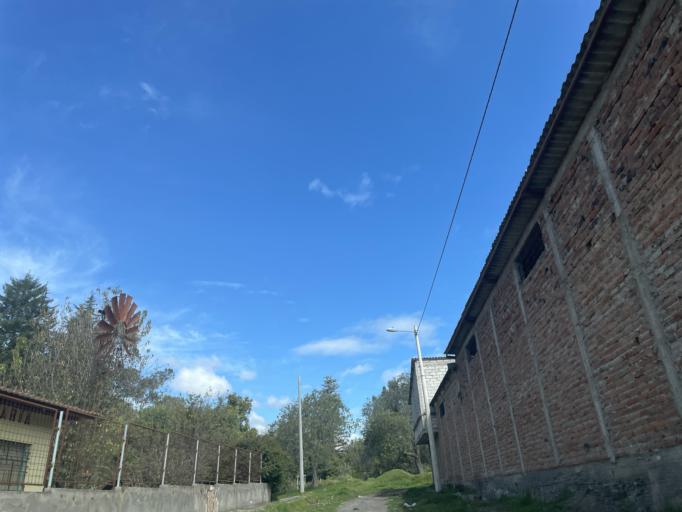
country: EC
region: Chimborazo
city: Guano
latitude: -1.6092
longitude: -78.6385
